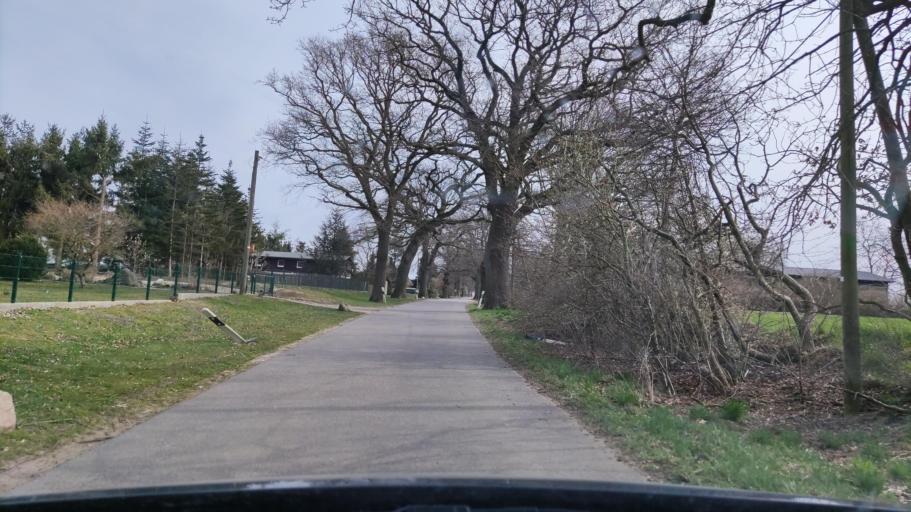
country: DE
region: Mecklenburg-Vorpommern
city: Robel
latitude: 53.3514
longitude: 12.5625
